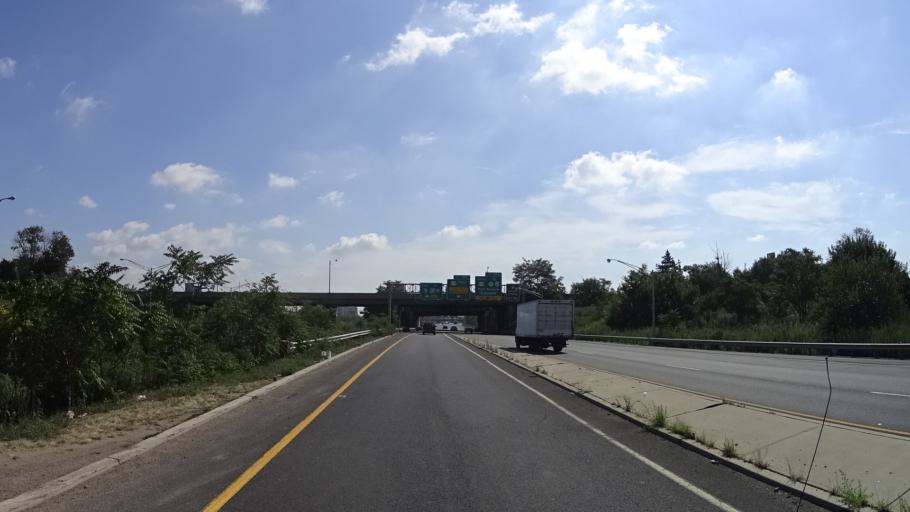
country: US
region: New Jersey
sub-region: Essex County
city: Newark
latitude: 40.7104
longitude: -74.1795
